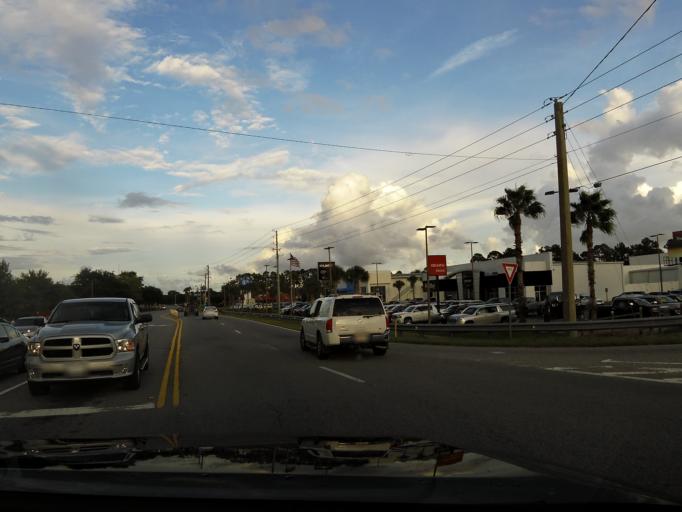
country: US
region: Georgia
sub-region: Glynn County
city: Country Club Estates
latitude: 31.2129
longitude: -81.4904
